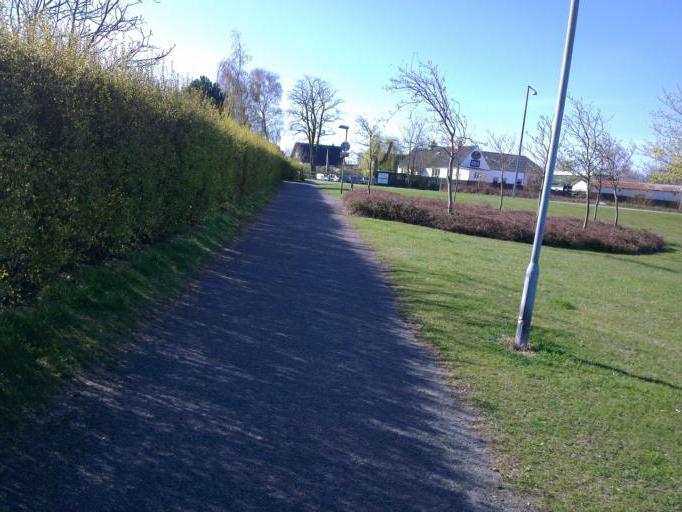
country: DK
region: Capital Region
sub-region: Frederikssund Kommune
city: Frederikssund
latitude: 55.8270
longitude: 12.0841
